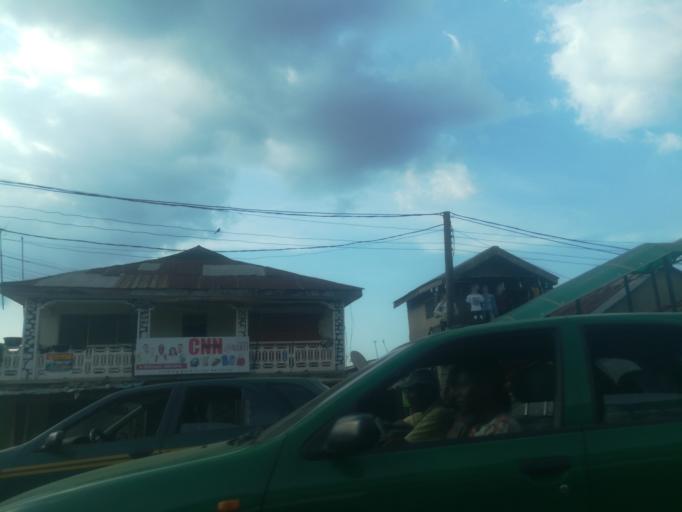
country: NG
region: Ogun
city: Abeokuta
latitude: 7.1344
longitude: 3.3309
